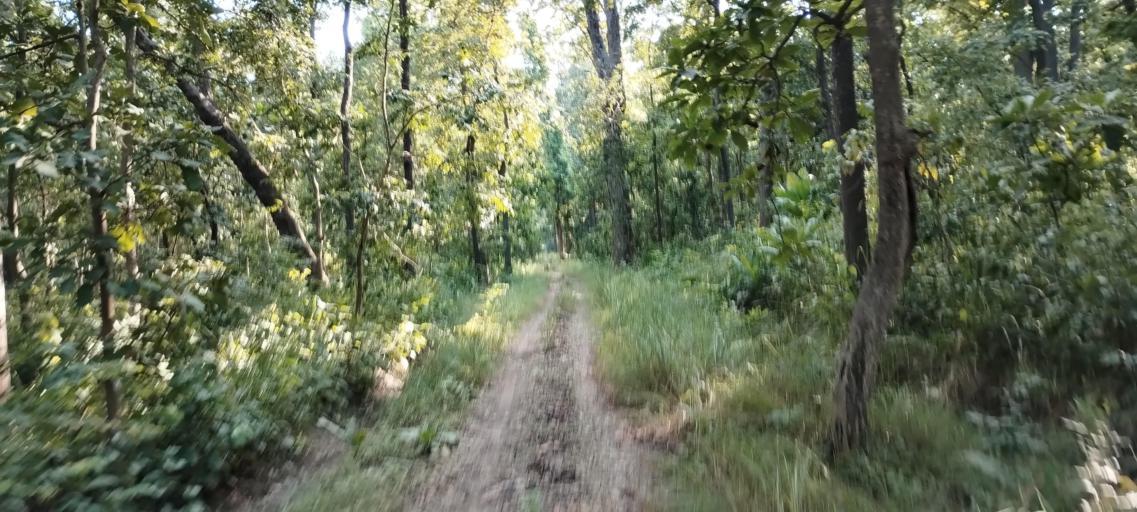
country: NP
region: Far Western
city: Tikapur
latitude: 28.5156
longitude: 81.2731
